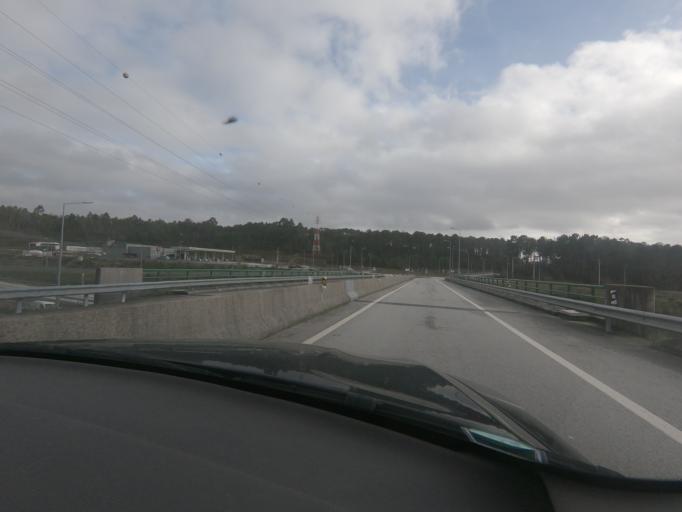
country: PT
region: Viseu
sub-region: Viseu
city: Campo
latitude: 40.7078
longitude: -7.9458
